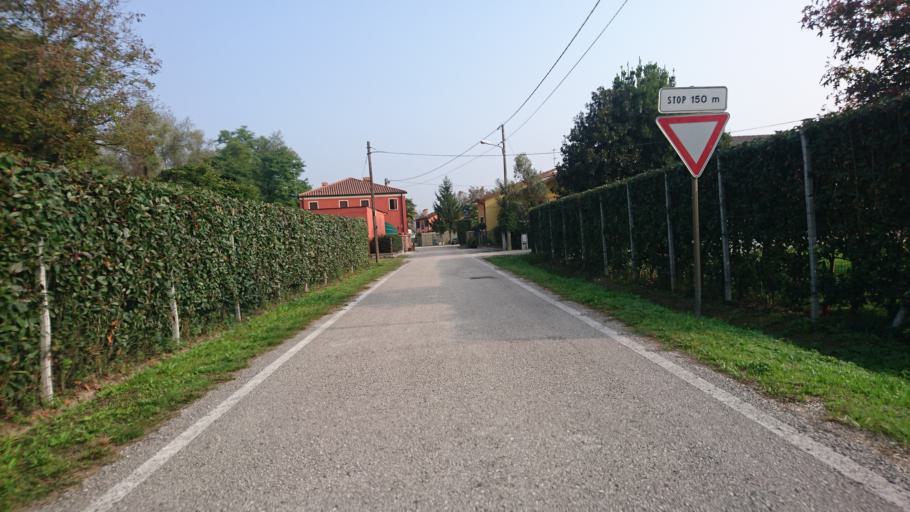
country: IT
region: Veneto
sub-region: Provincia di Padova
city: Santa Maria di Non
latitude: 45.5160
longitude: 11.8450
